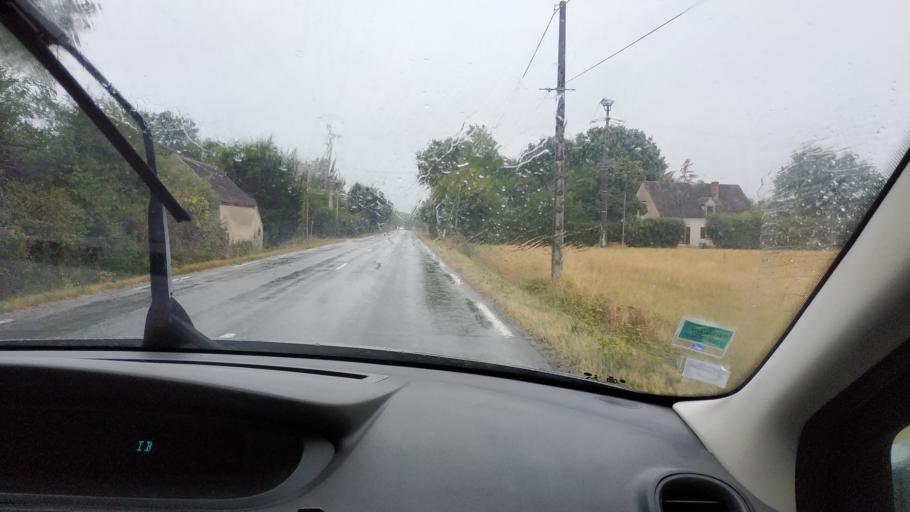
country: FR
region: Centre
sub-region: Departement du Loiret
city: Bellegarde
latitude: 47.9456
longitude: 2.3812
